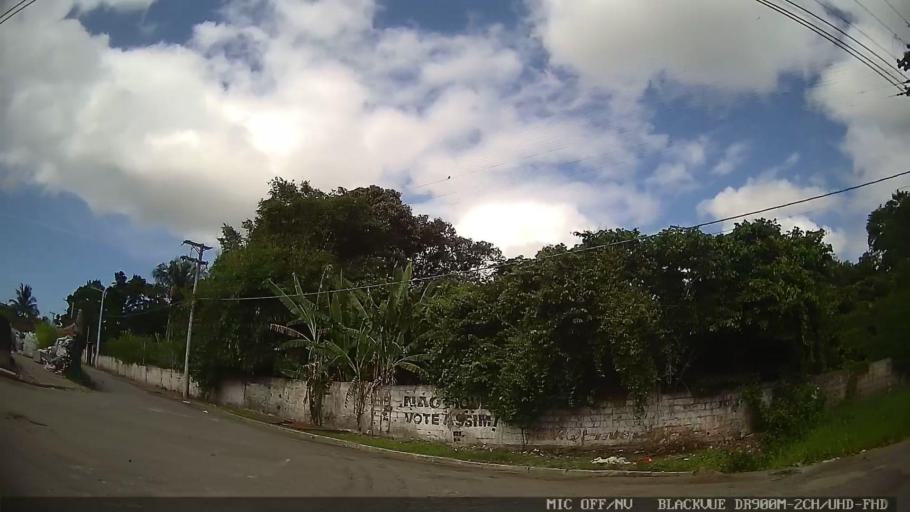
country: BR
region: Sao Paulo
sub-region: Peruibe
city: Peruibe
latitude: -24.2991
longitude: -47.0271
